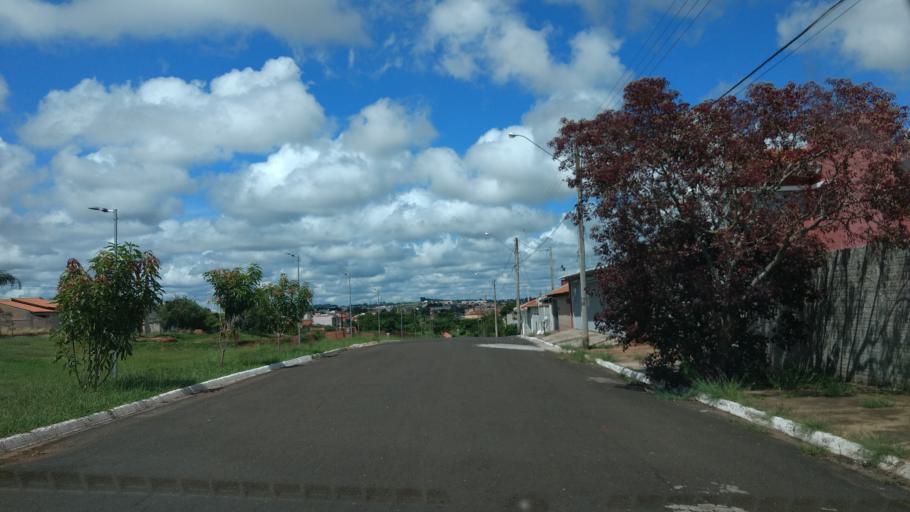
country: BR
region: Sao Paulo
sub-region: Botucatu
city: Botucatu
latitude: -22.8537
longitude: -48.4414
